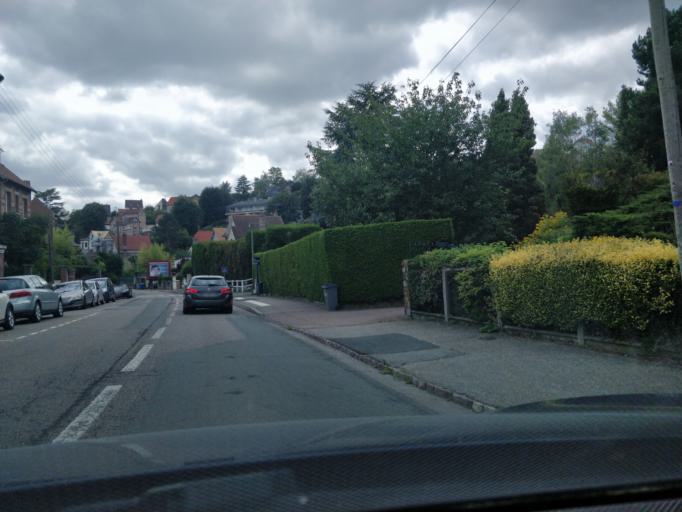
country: FR
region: Haute-Normandie
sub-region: Departement de la Seine-Maritime
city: Mont-Saint-Aignan
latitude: 49.4606
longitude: 1.0941
